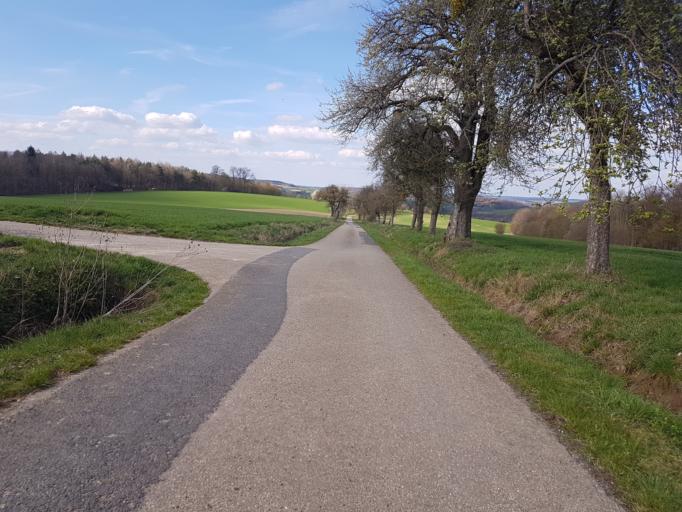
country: DE
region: Baden-Wuerttemberg
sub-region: Regierungsbezirk Stuttgart
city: Forchtenberg
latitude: 49.3309
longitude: 9.5276
